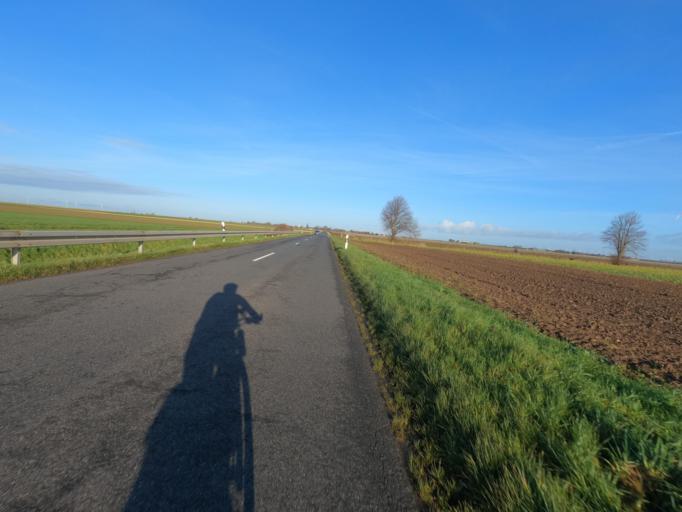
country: DE
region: North Rhine-Westphalia
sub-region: Regierungsbezirk Koln
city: Titz
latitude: 50.9652
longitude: 6.4114
